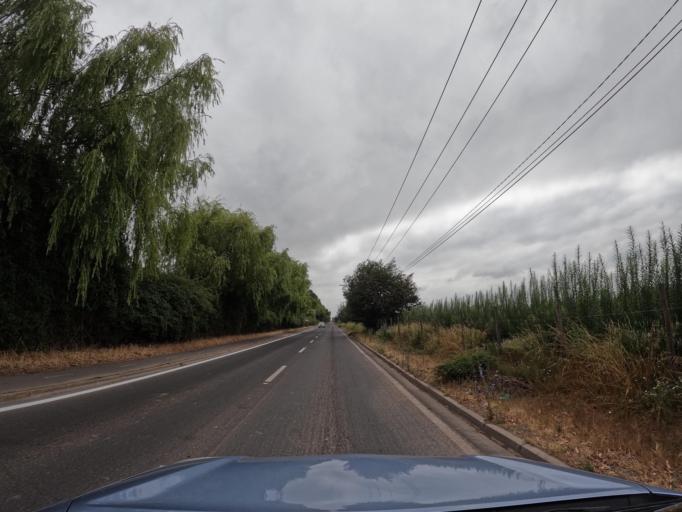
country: CL
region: O'Higgins
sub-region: Provincia de Colchagua
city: Chimbarongo
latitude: -34.7298
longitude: -71.0594
